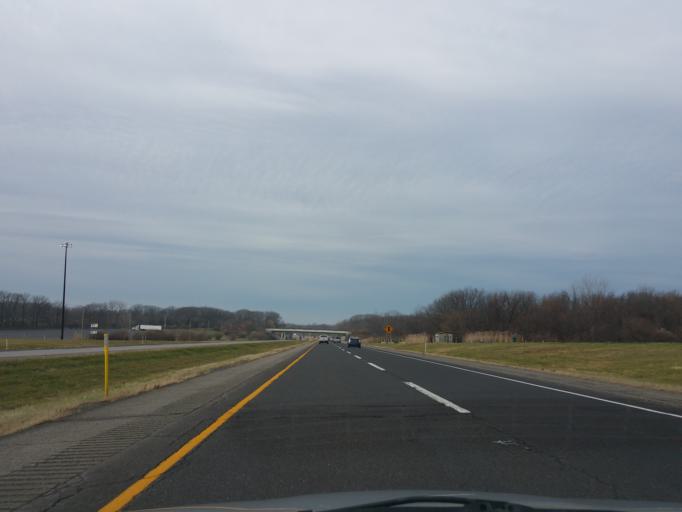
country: US
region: Indiana
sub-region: LaPorte County
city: Westville
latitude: 41.5866
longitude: -86.9245
